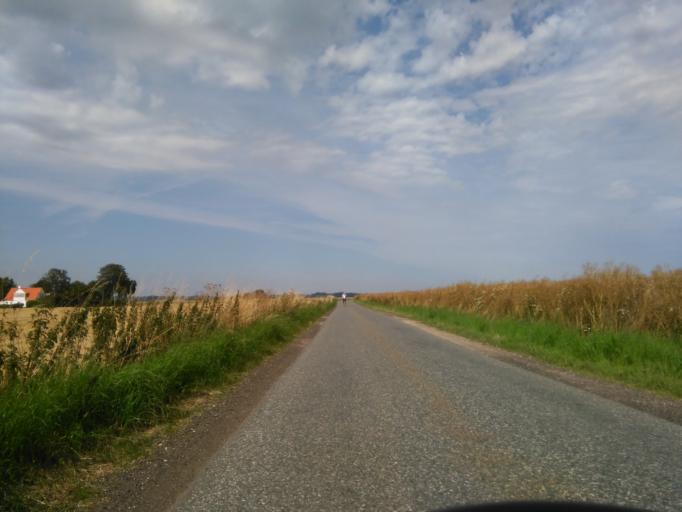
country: DK
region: Central Jutland
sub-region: Hedensted Kommune
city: Juelsminde
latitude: 55.8525
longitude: 10.0475
